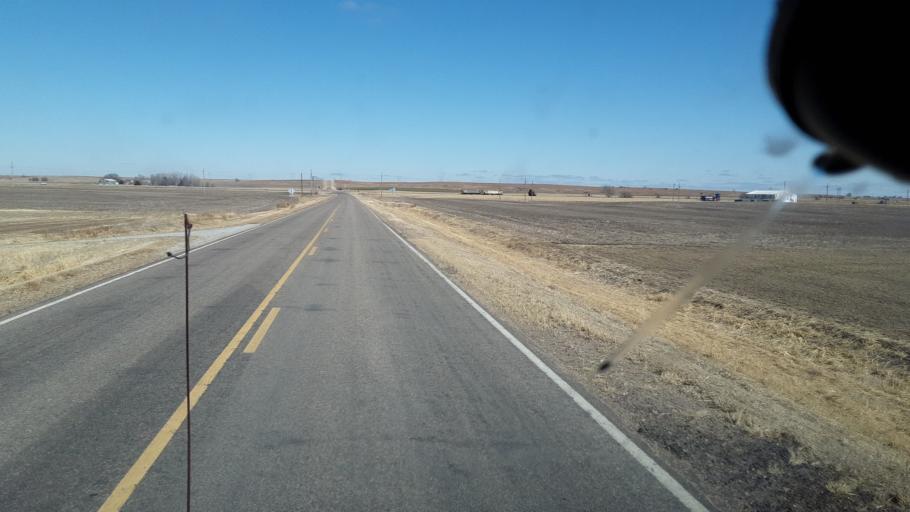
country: US
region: Kansas
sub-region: Barton County
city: Ellinwood
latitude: 38.3587
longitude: -98.6640
